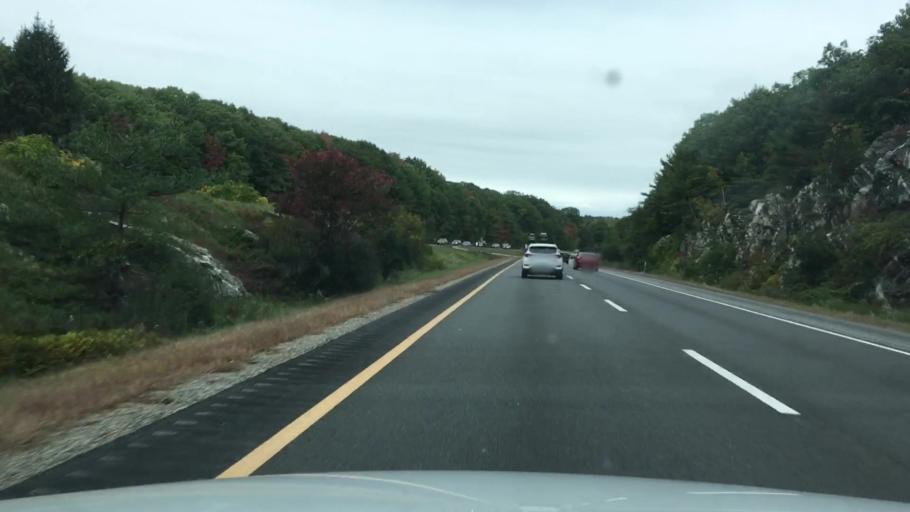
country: US
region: Maine
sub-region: Cumberland County
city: Falmouth
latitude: 43.7069
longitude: -70.2555
